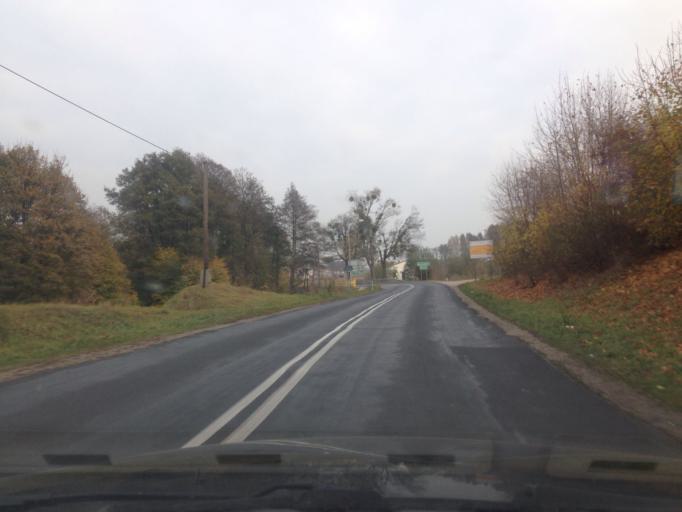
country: PL
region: Kujawsko-Pomorskie
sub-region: Powiat brodnicki
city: Brodnica
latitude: 53.2534
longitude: 19.4335
